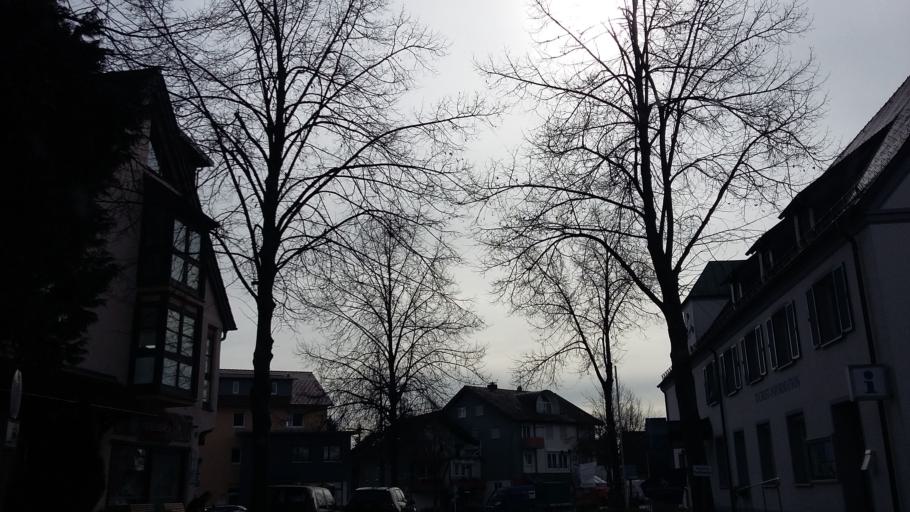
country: DE
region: Bavaria
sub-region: Swabia
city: Bodolz
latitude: 47.5709
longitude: 9.6387
